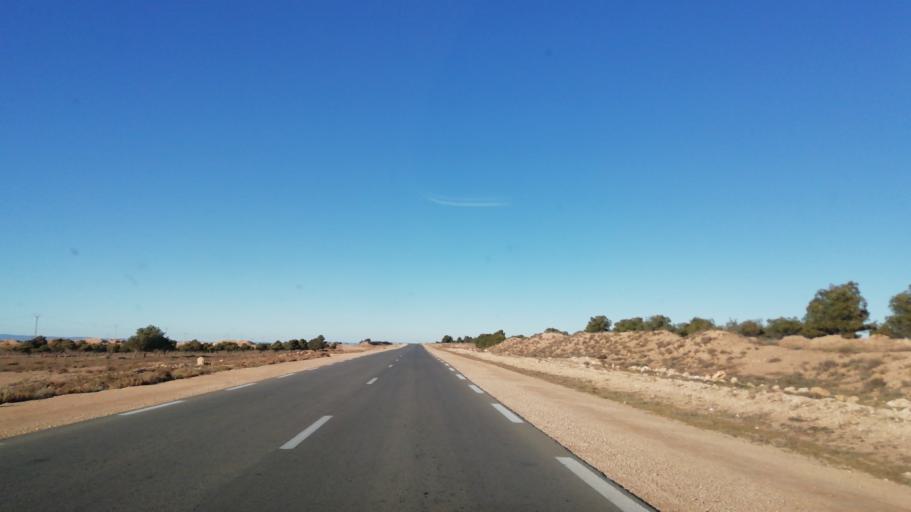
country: DZ
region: Tlemcen
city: Sebdou
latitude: 34.2743
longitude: -1.2586
